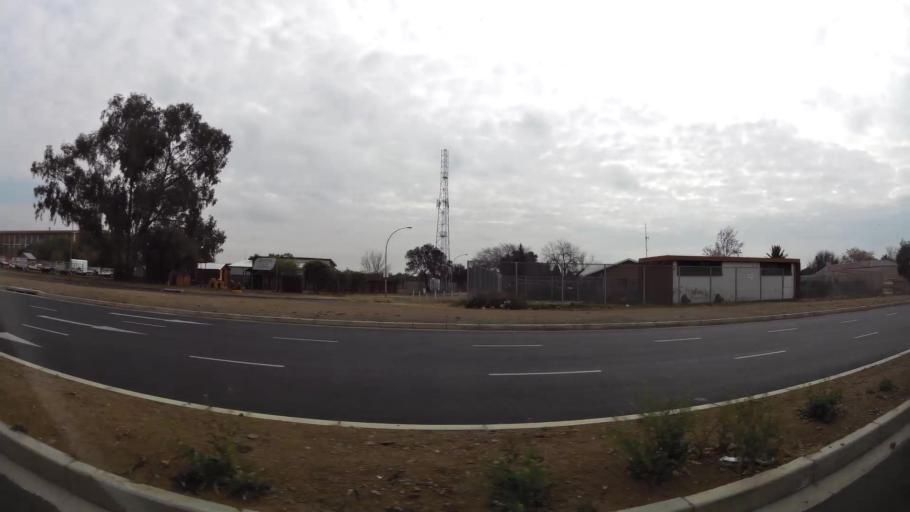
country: ZA
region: Orange Free State
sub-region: Mangaung Metropolitan Municipality
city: Bloemfontein
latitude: -29.1258
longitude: 26.1930
